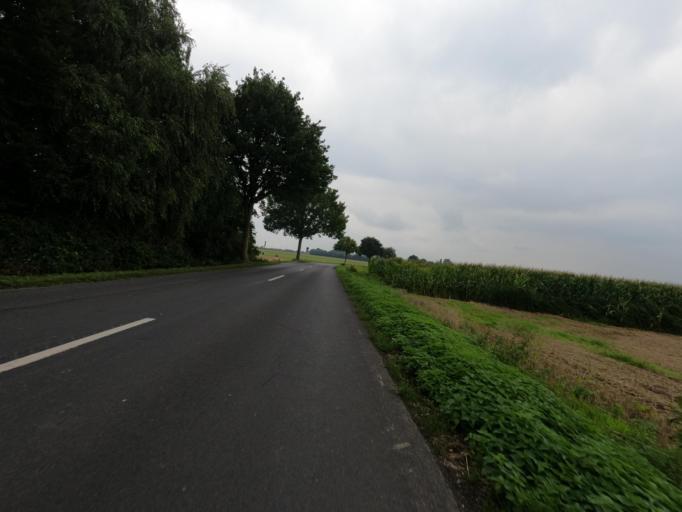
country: DE
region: North Rhine-Westphalia
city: Baesweiler
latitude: 50.9270
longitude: 6.1772
